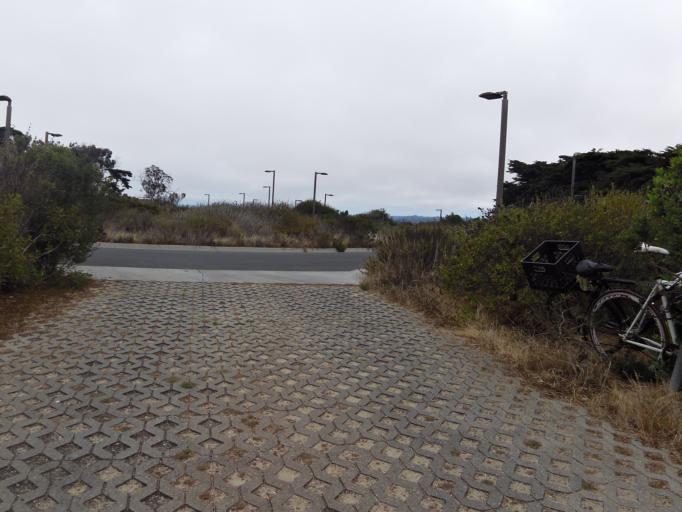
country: US
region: California
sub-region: Monterey County
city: Castroville
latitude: 36.7936
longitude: -121.7874
